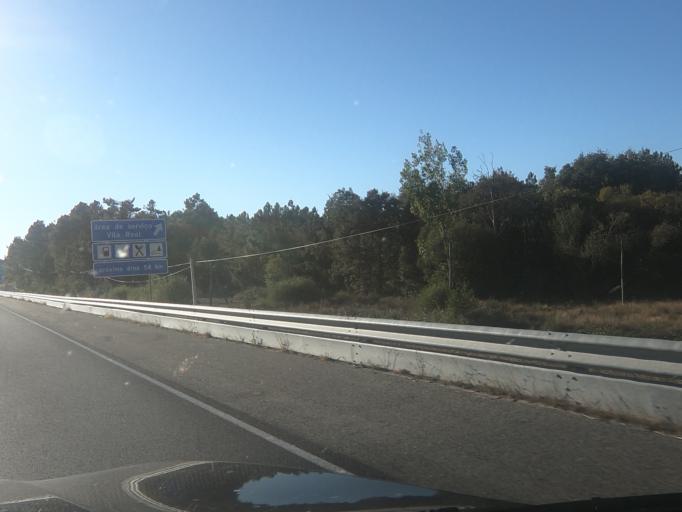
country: PT
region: Vila Real
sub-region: Sabrosa
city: Sabrosa
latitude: 41.3255
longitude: -7.6331
